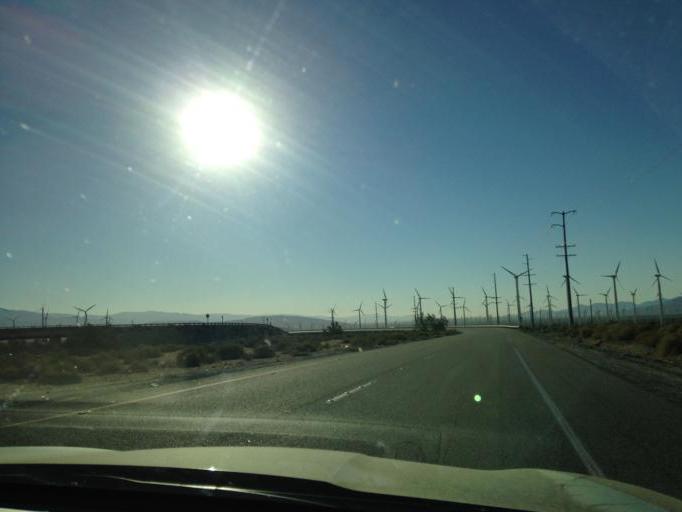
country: US
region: California
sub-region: Riverside County
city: Garnet
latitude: 33.9152
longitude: -116.6109
